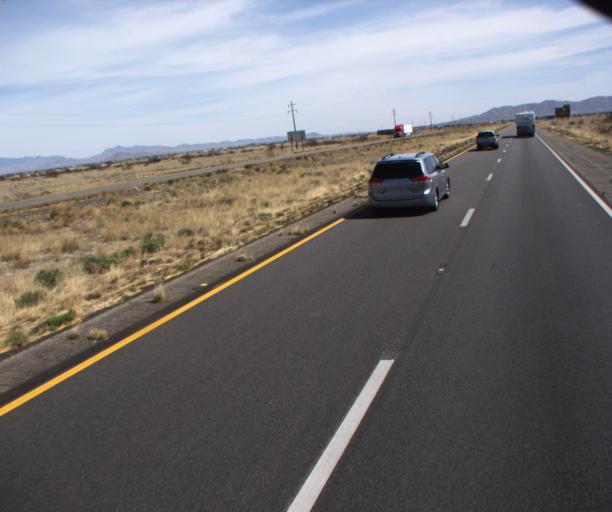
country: US
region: Arizona
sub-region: Cochise County
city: Willcox
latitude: 32.2095
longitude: -109.8936
